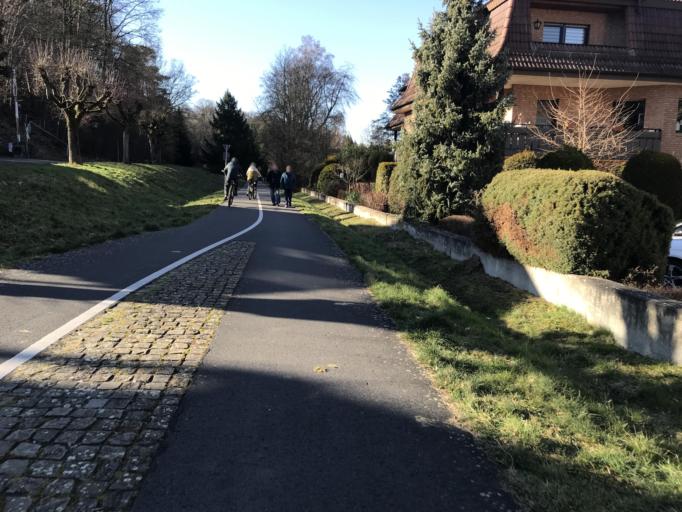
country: DE
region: Hesse
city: Neukirchen
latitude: 50.8652
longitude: 9.3439
